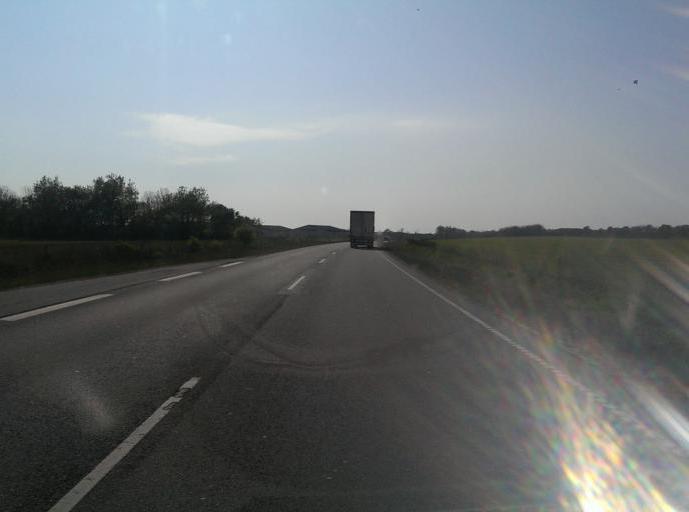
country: DK
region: South Denmark
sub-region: Esbjerg Kommune
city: Esbjerg
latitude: 55.5166
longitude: 8.4810
